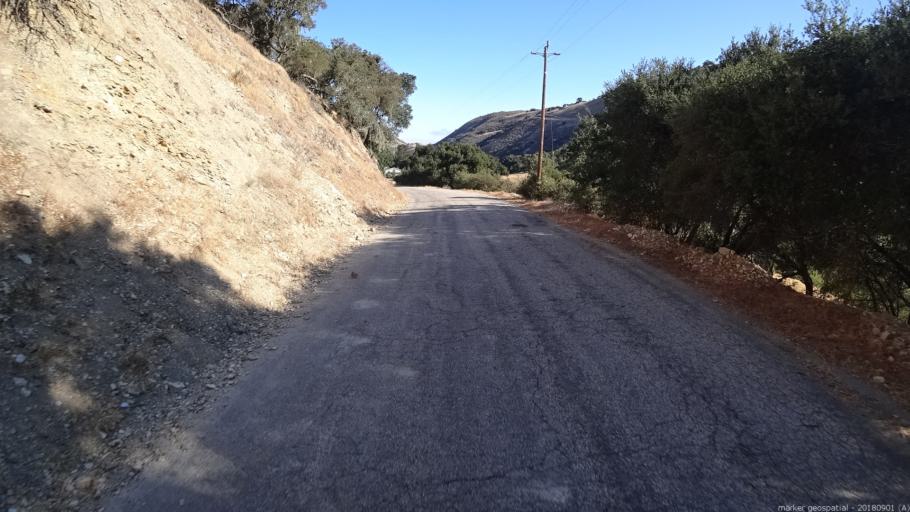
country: US
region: California
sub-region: Monterey County
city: Greenfield
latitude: 36.2027
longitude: -121.2765
